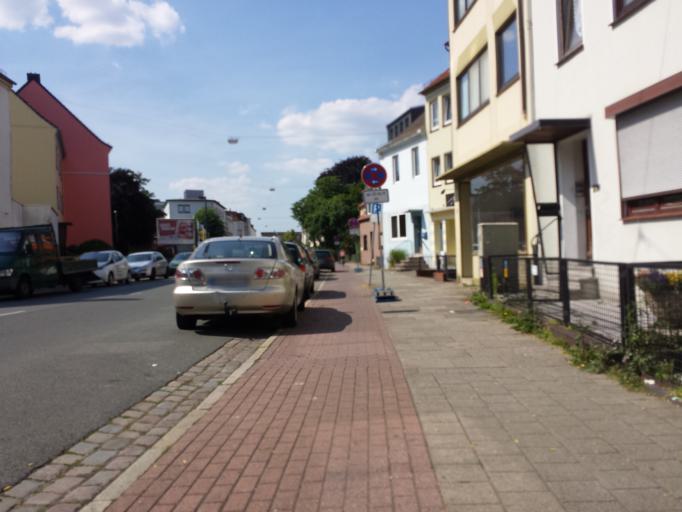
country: DE
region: Bremen
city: Bremen
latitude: 53.0851
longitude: 8.7652
